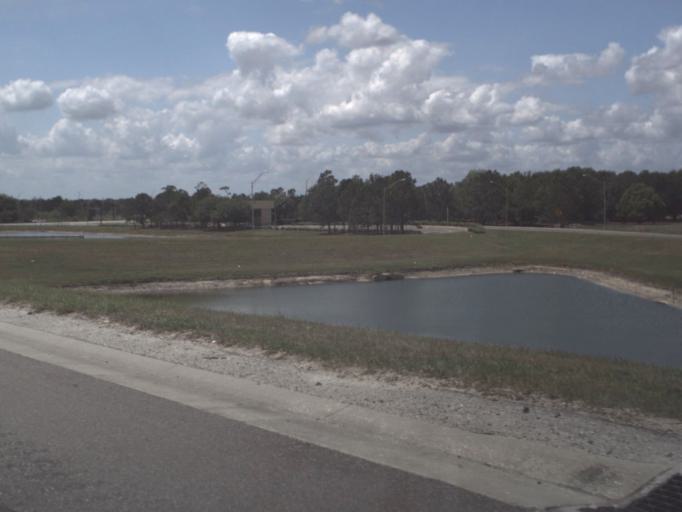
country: US
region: Florida
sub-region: Orange County
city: Ocoee
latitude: 28.5757
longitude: -81.5572
